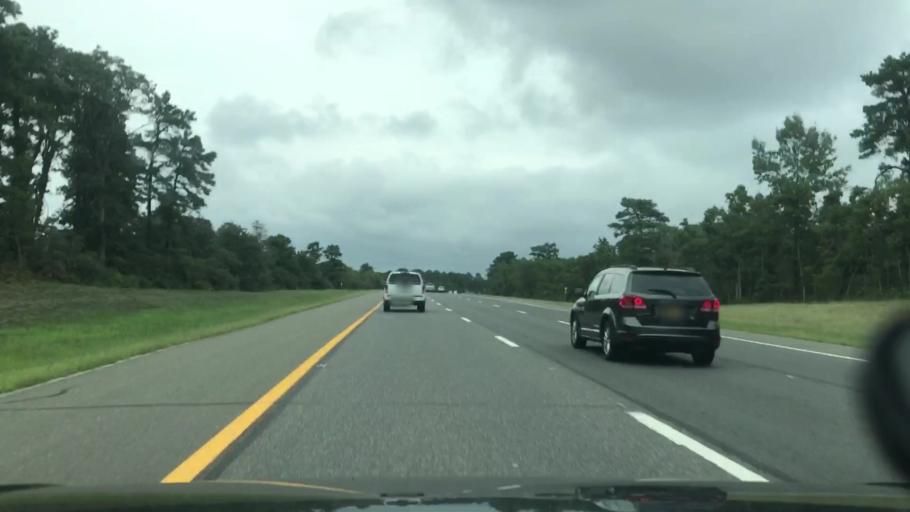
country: US
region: New Jersey
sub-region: Ocean County
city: Waretown
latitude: 39.8079
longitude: -74.2311
